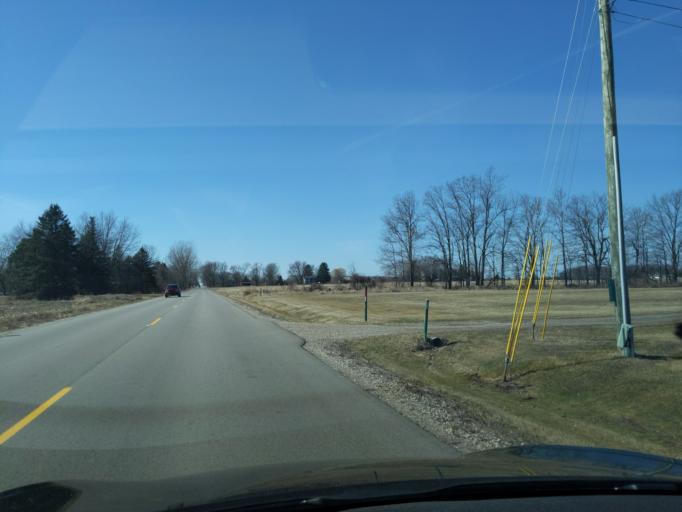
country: US
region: Michigan
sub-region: Eaton County
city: Grand Ledge
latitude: 42.7265
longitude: -84.8123
